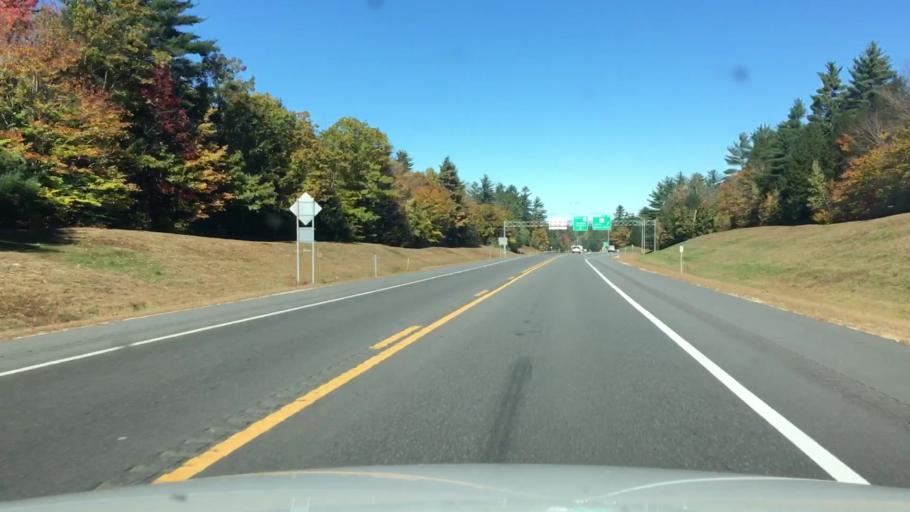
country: US
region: New Hampshire
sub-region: Carroll County
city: Sanbornville
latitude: 43.4740
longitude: -71.0021
